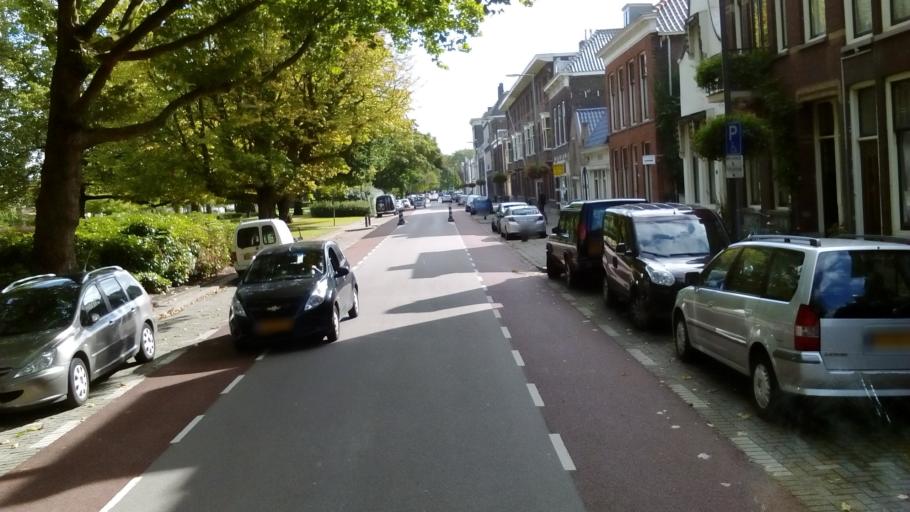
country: NL
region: South Holland
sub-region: Gemeente Schiedam
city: Schiedam
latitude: 51.9124
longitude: 4.4018
